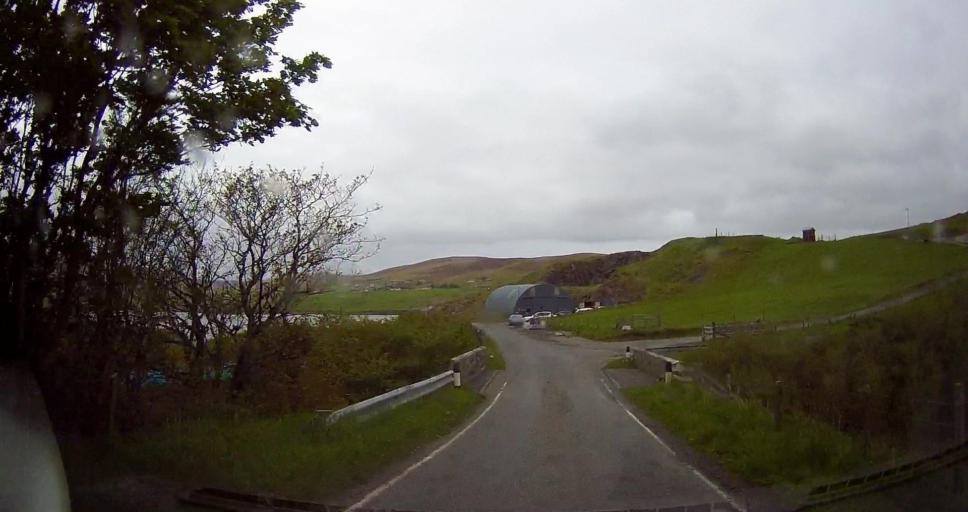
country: GB
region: Scotland
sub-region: Shetland Islands
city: Lerwick
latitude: 60.3457
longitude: -1.2724
